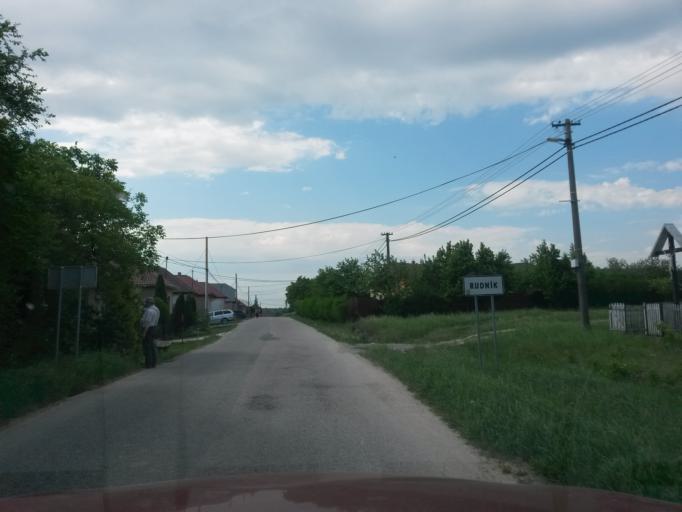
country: SK
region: Kosicky
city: Moldava nad Bodvou
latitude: 48.6968
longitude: 21.0119
